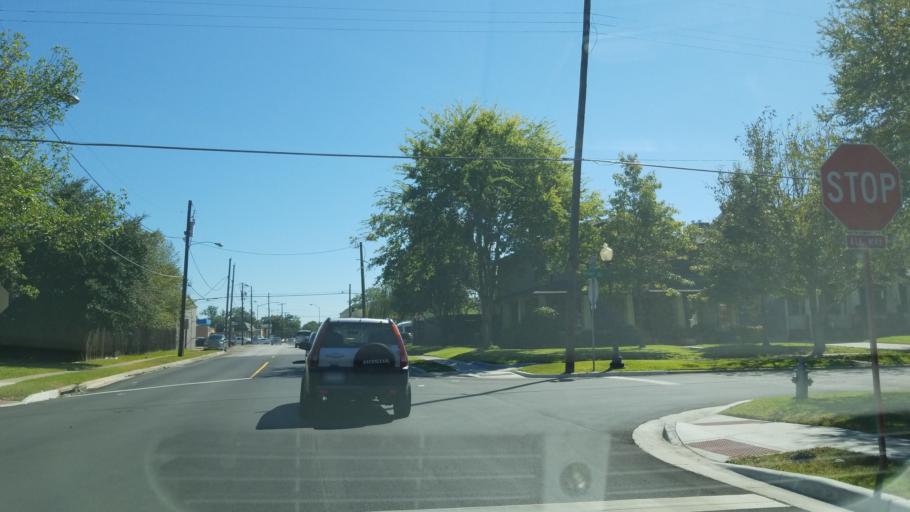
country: US
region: Texas
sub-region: Dallas County
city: Highland Park
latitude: 32.7978
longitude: -96.7633
